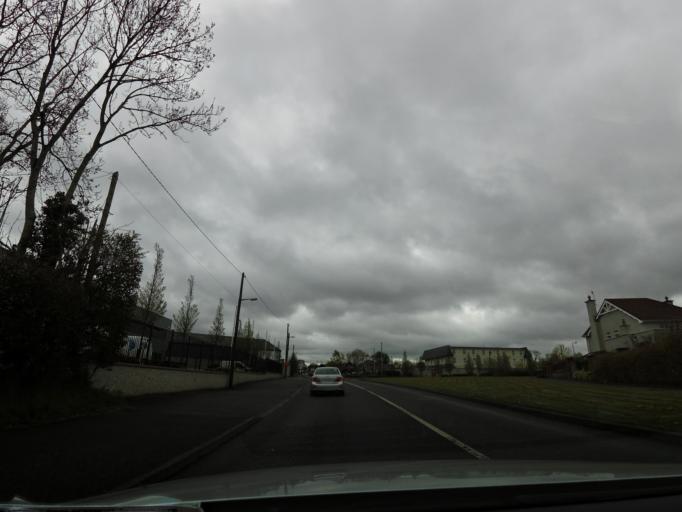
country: IE
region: Leinster
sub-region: Kilkenny
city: Kilkenny
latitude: 52.6688
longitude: -7.2661
